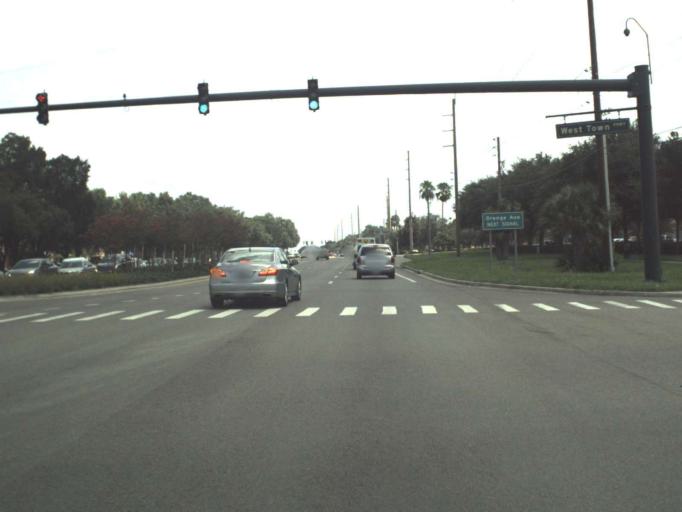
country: US
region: Florida
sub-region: Seminole County
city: Forest City
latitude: 28.6582
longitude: -81.4192
